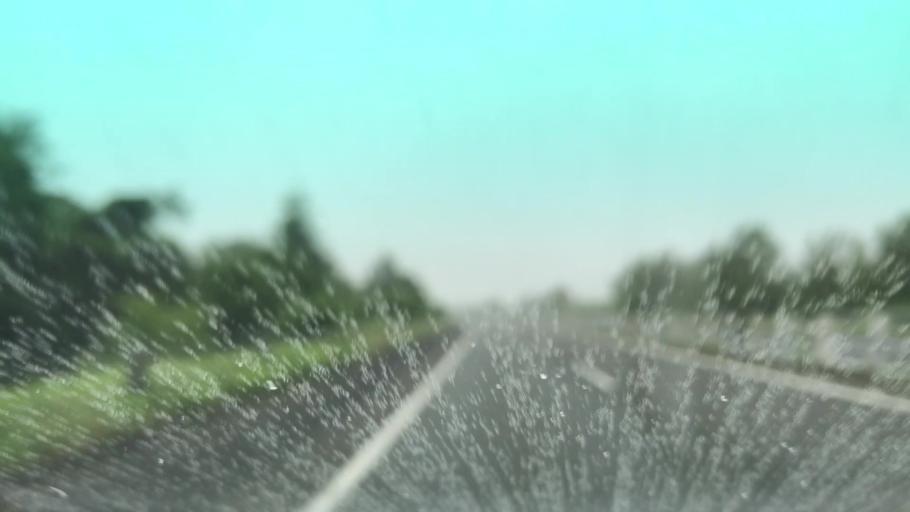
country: JP
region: Hokkaido
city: Shiraoi
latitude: 42.5250
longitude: 141.2688
